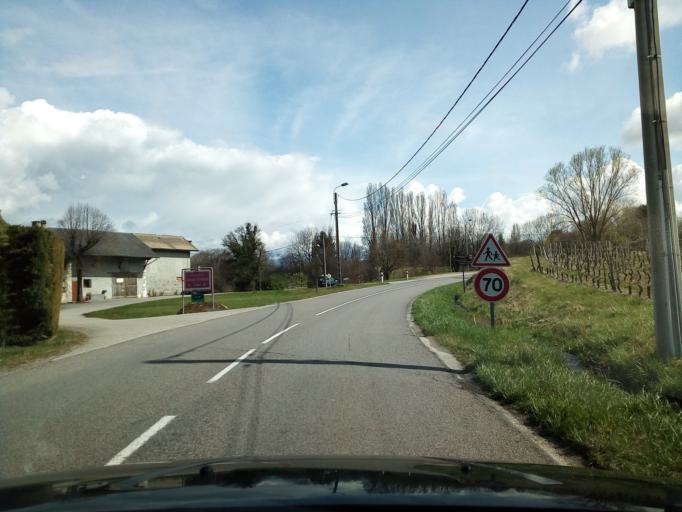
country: FR
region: Rhone-Alpes
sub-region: Departement de la Savoie
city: Saint-Baldoph
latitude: 45.5042
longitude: 5.9641
